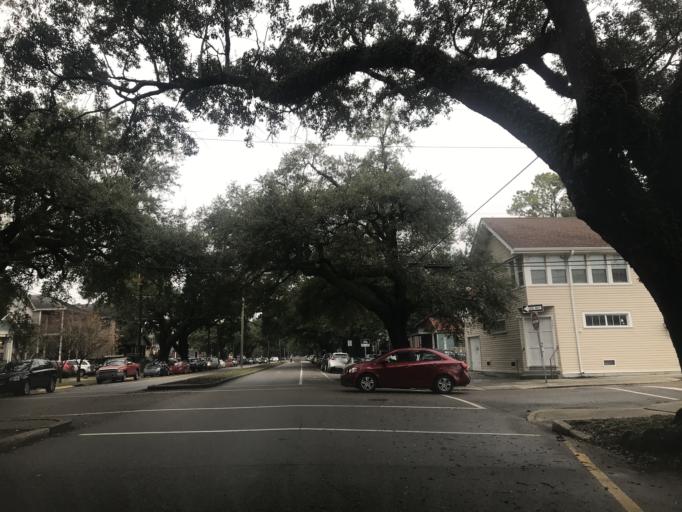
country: US
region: Louisiana
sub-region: Orleans Parish
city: New Orleans
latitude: 29.9736
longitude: -90.1054
